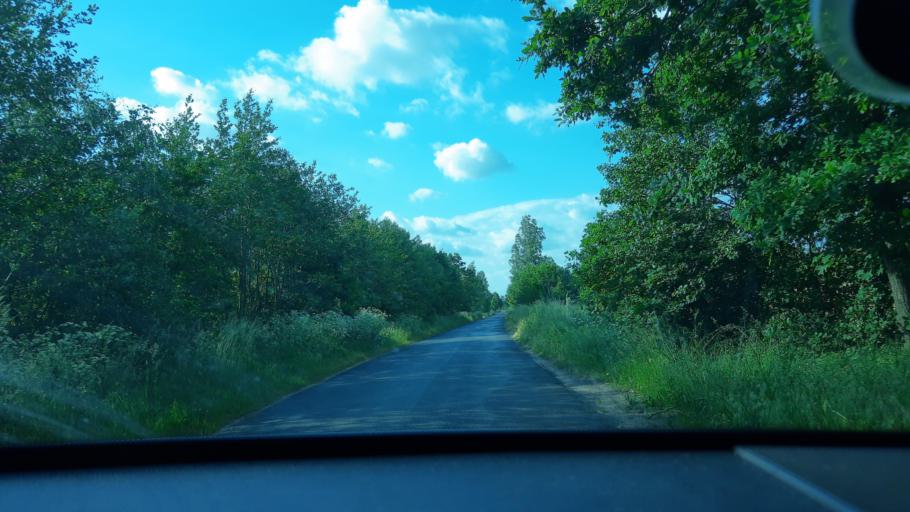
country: PL
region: Lodz Voivodeship
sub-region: Powiat zdunskowolski
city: Zapolice
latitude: 51.5305
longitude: 18.8374
